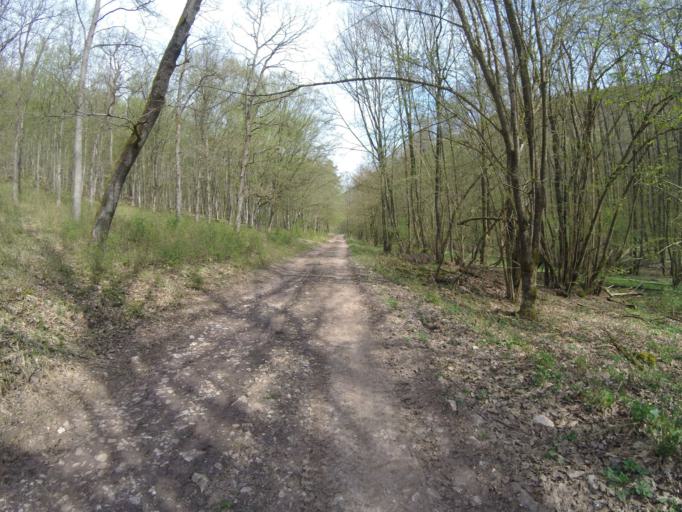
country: HU
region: Borsod-Abauj-Zemplen
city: Rudabanya
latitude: 48.5306
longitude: 20.6380
